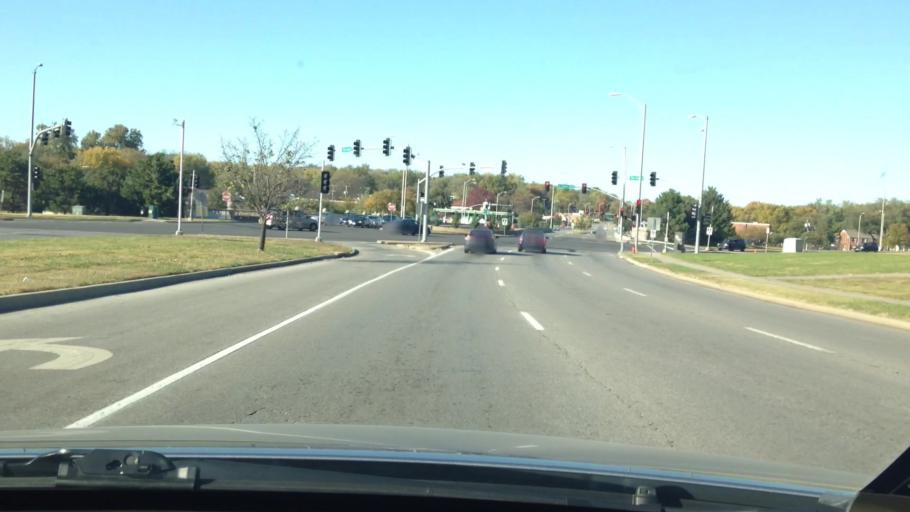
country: US
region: Kansas
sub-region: Johnson County
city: Westwood
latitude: 39.0392
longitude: -94.5681
